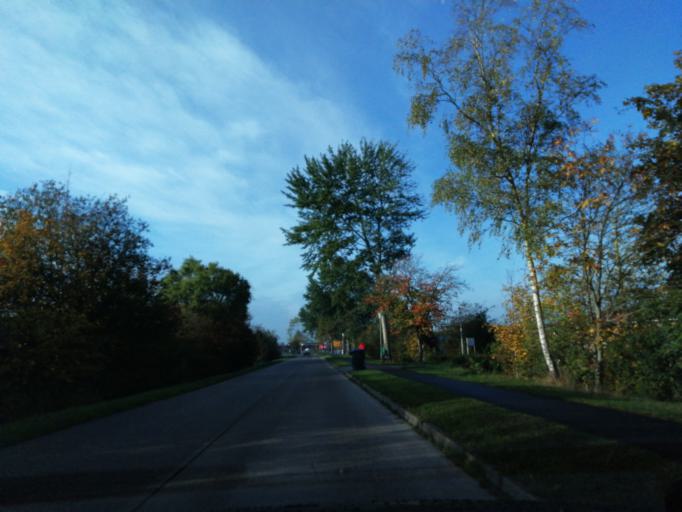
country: DE
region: Lower Saxony
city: Schillig
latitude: 53.6354
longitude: 8.0195
